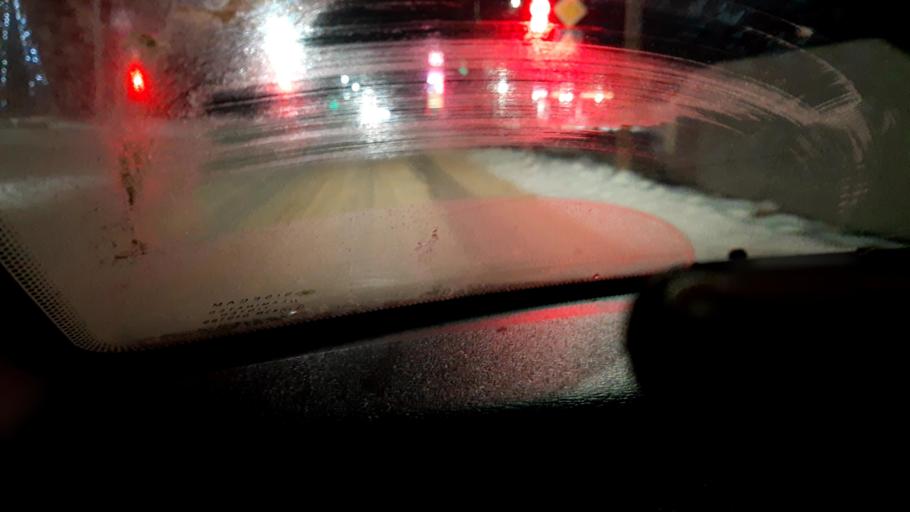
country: RU
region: Nizjnij Novgorod
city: Bogorodsk
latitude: 56.0981
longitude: 43.4799
